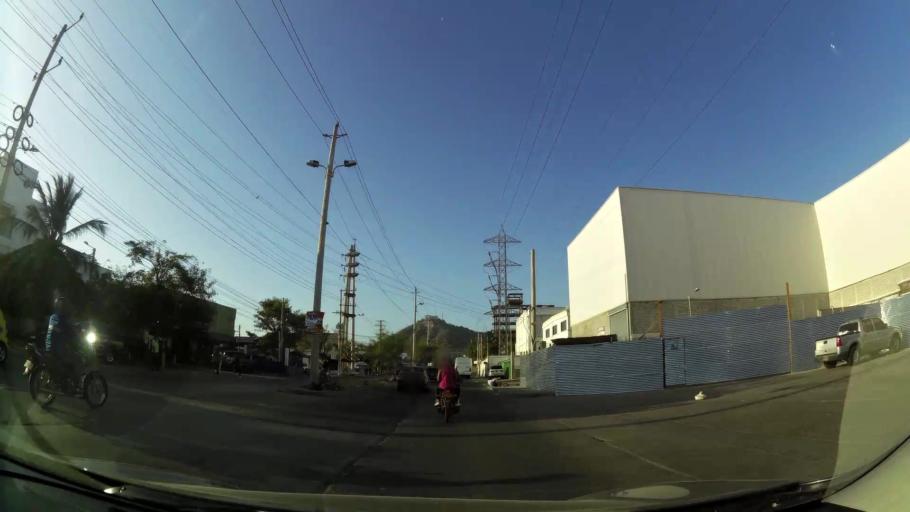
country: CO
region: Bolivar
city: Cartagena
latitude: 10.4085
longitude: -75.5214
